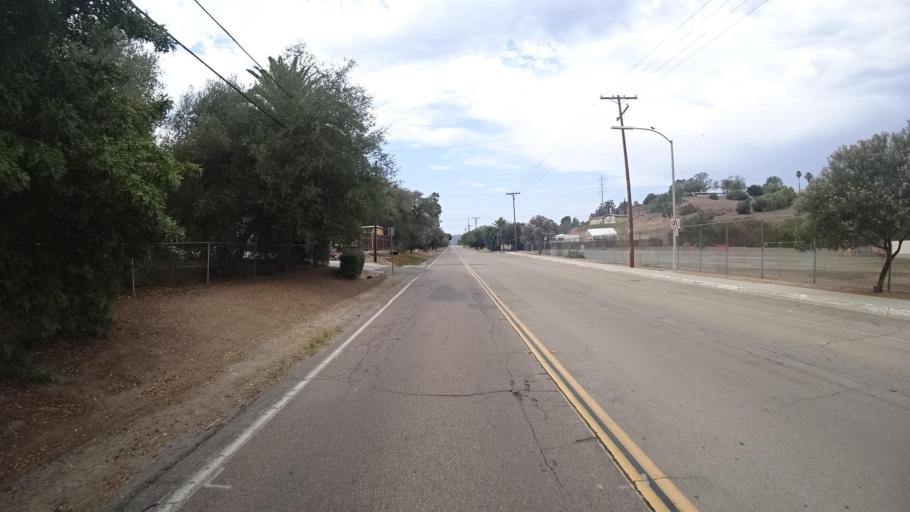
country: US
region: California
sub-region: San Diego County
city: Escondido
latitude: 33.1371
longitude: -117.1081
